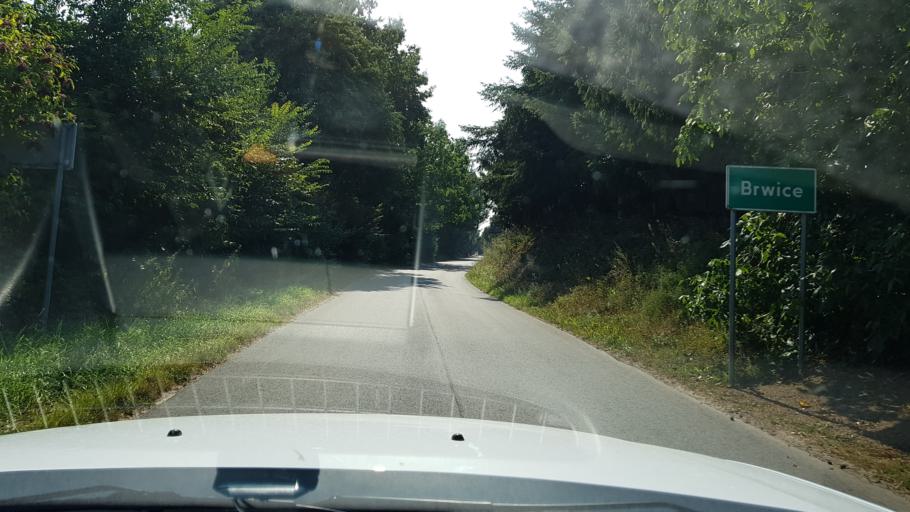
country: PL
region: West Pomeranian Voivodeship
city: Trzcinsko Zdroj
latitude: 52.9241
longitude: 14.5320
